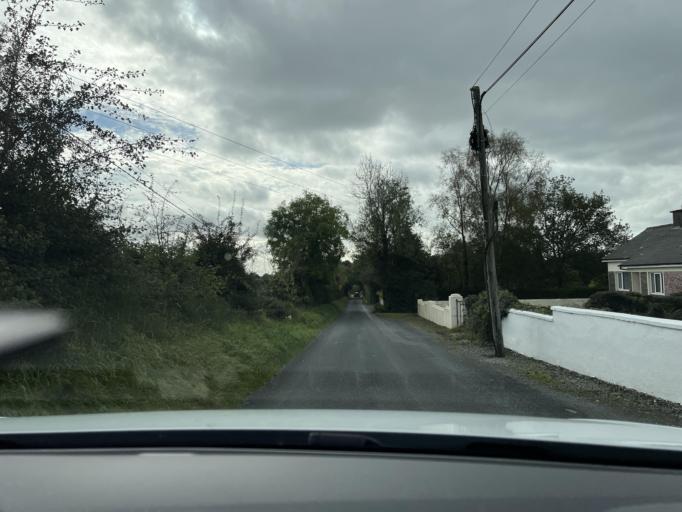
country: IE
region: Connaught
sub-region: County Leitrim
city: Carrick-on-Shannon
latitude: 53.9635
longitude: -8.0855
